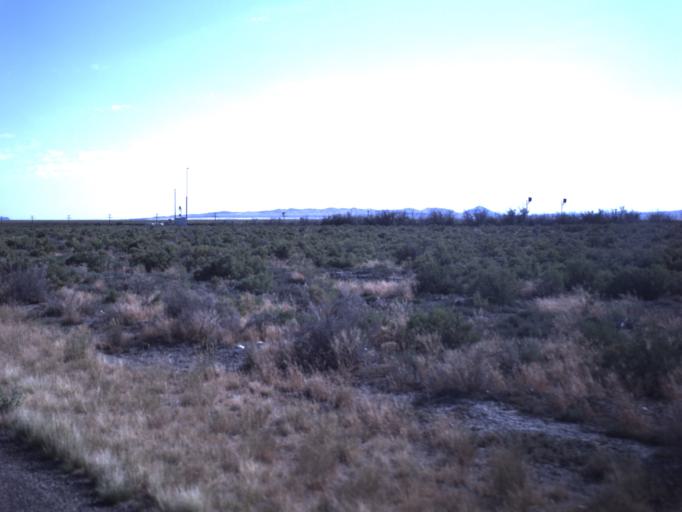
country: US
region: Utah
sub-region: Beaver County
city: Milford
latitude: 38.5986
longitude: -112.9875
